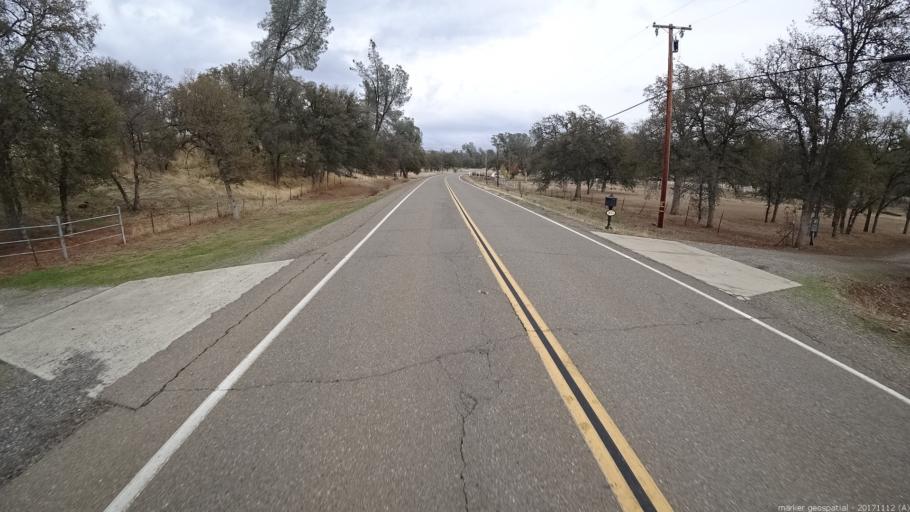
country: US
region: California
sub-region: Shasta County
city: Palo Cedro
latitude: 40.4874
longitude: -122.1404
